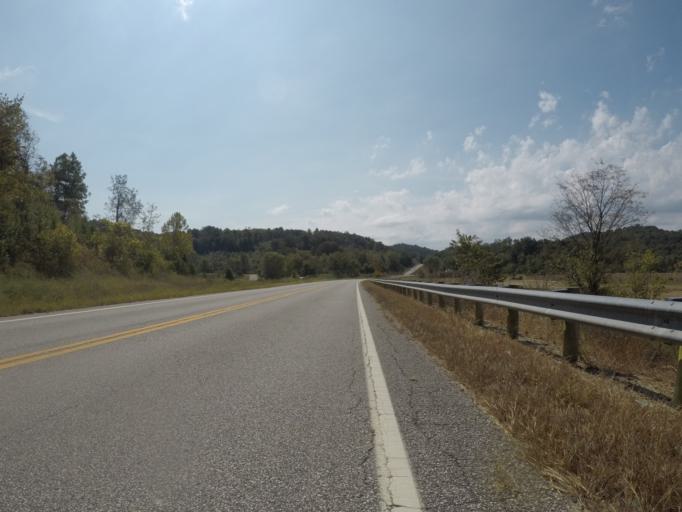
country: US
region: West Virginia
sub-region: Cabell County
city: Lesage
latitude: 38.5106
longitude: -82.3922
